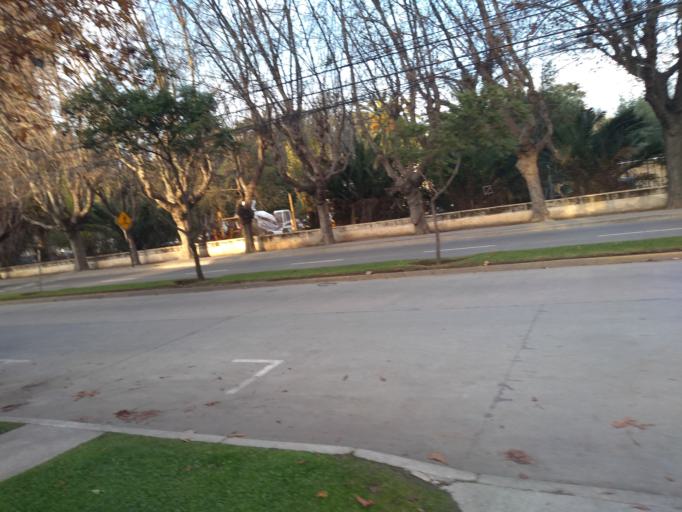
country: CL
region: Valparaiso
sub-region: Provincia de Valparaiso
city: Vina del Mar
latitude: -33.0197
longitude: -71.5411
